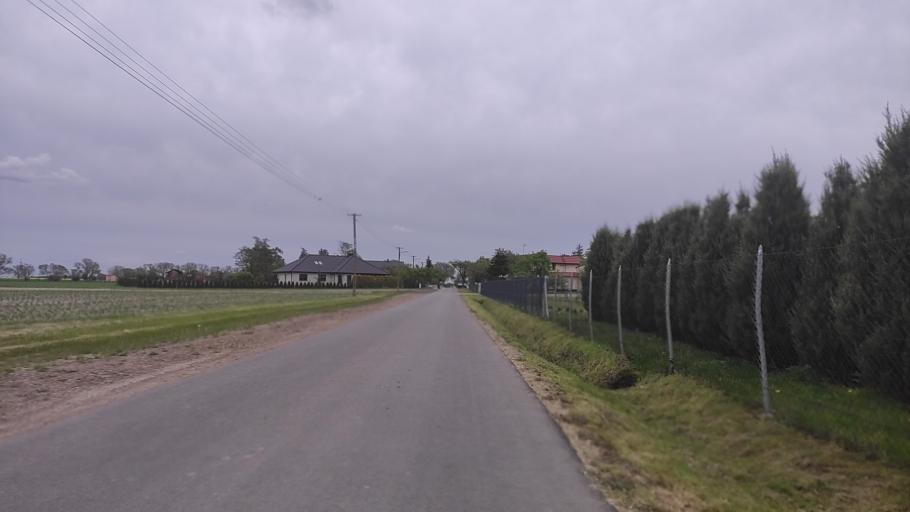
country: PL
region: Greater Poland Voivodeship
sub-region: Powiat poznanski
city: Swarzedz
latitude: 52.4105
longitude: 17.1298
